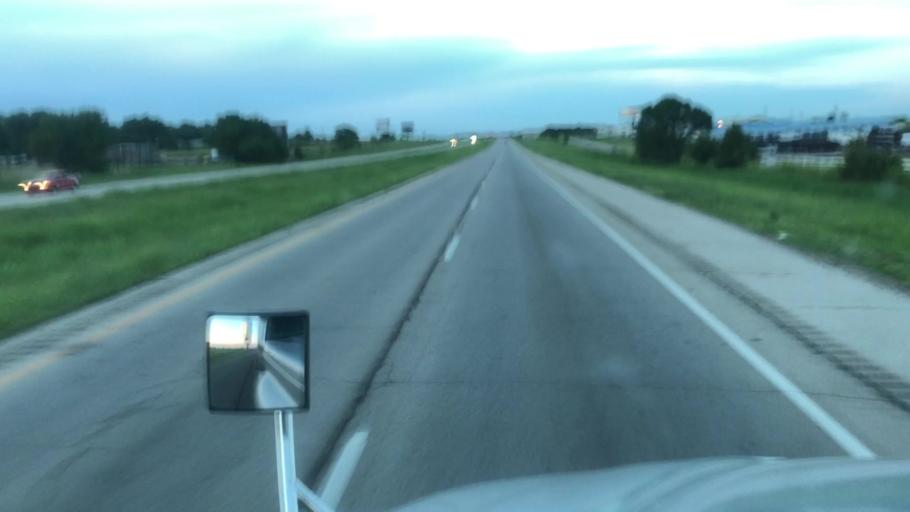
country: US
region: Oklahoma
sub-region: Kay County
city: Ponca City
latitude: 36.7550
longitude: -97.0653
